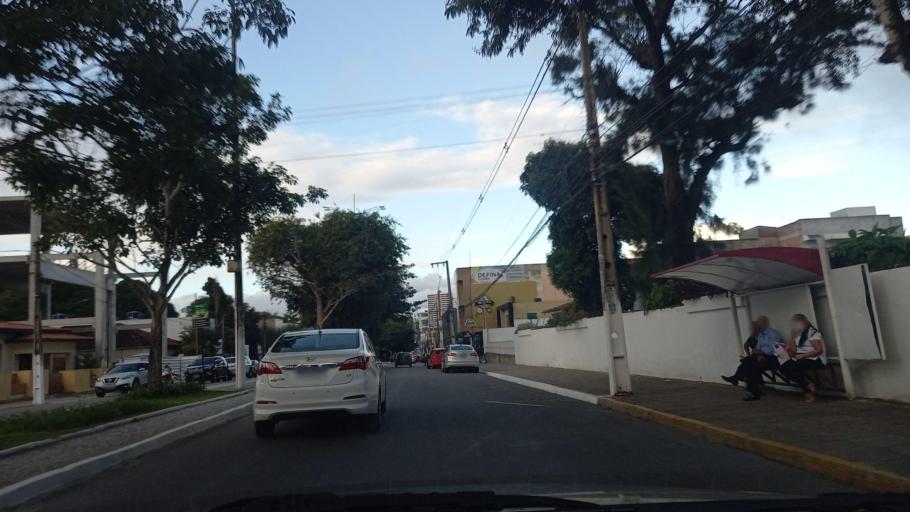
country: BR
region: Pernambuco
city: Garanhuns
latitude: -8.8857
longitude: -36.4845
